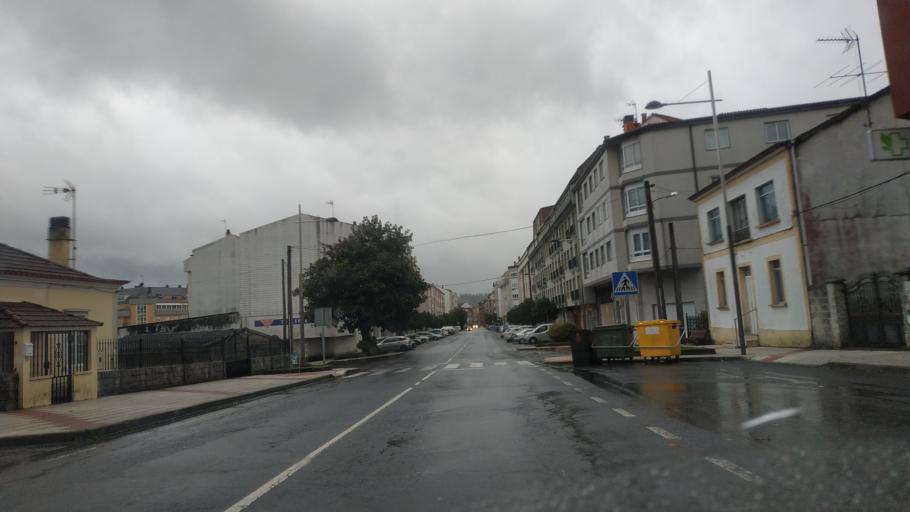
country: ES
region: Galicia
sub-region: Provincia da Coruna
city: Negreira
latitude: 42.9147
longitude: -8.7356
